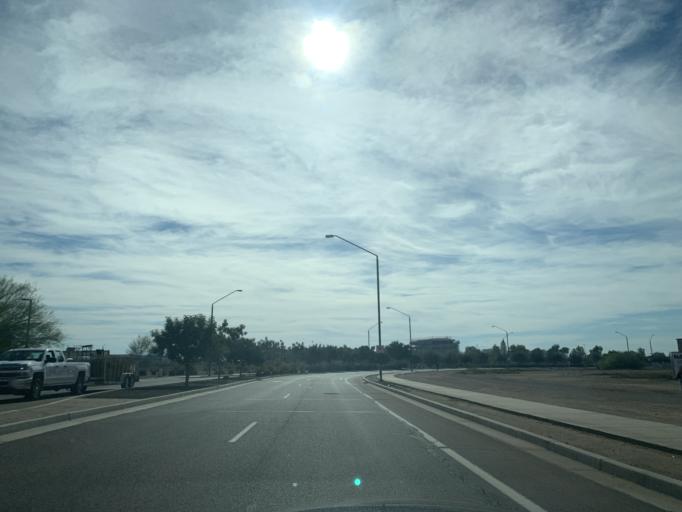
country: US
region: Arizona
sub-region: Maricopa County
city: Gilbert
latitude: 33.2941
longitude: -111.7498
